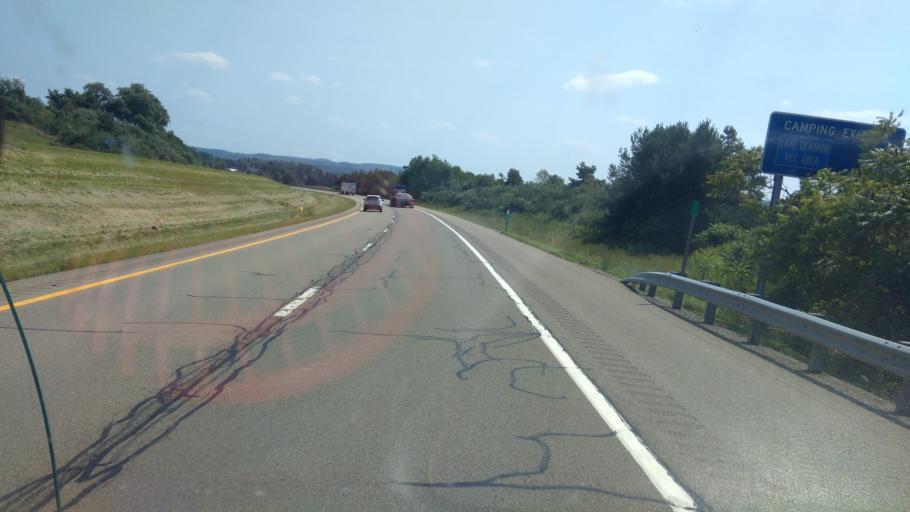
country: US
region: New York
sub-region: Steuben County
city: Canisteo
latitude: 42.3698
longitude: -77.5211
